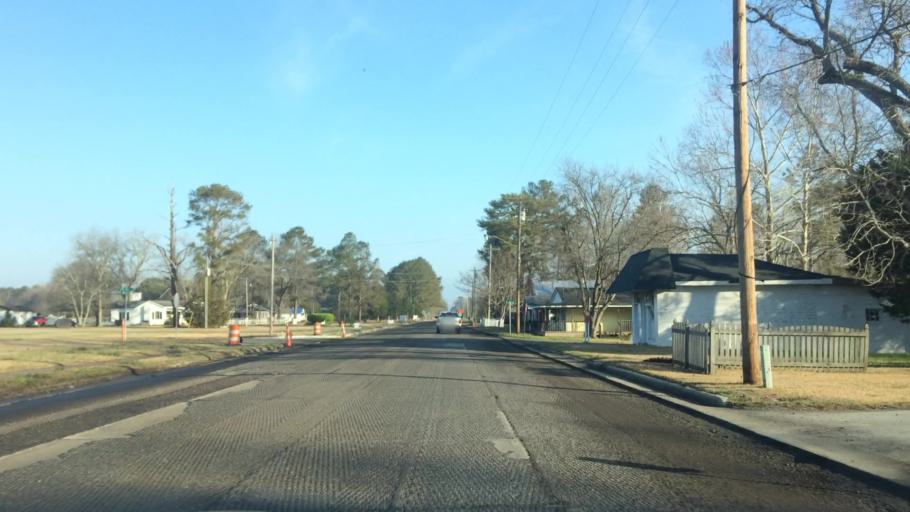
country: US
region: North Carolina
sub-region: Pitt County
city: Farmville
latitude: 35.6755
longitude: -77.6404
